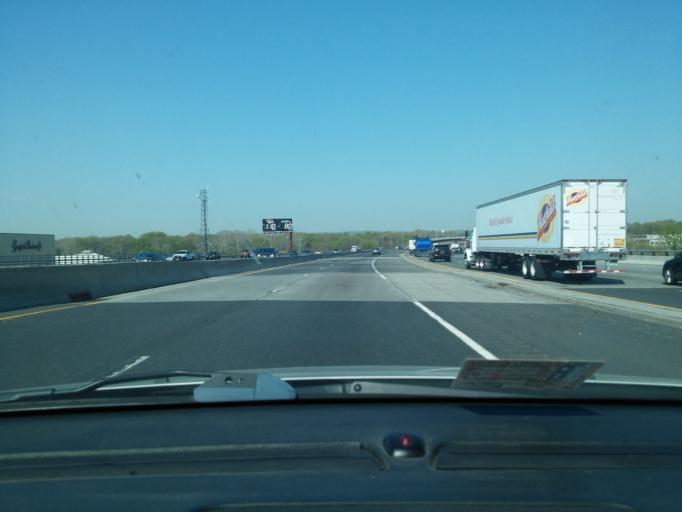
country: US
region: New Jersey
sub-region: Union County
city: Hillside
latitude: 40.7051
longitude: -74.2408
